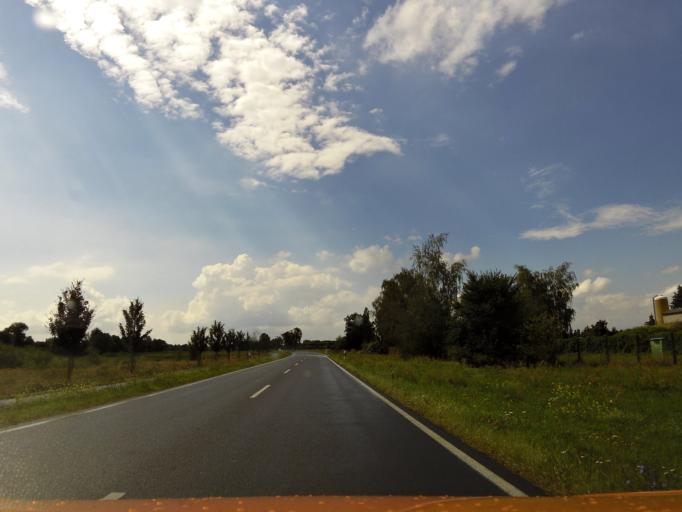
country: DE
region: Brandenburg
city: Ketzin
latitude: 52.4891
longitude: 12.8676
